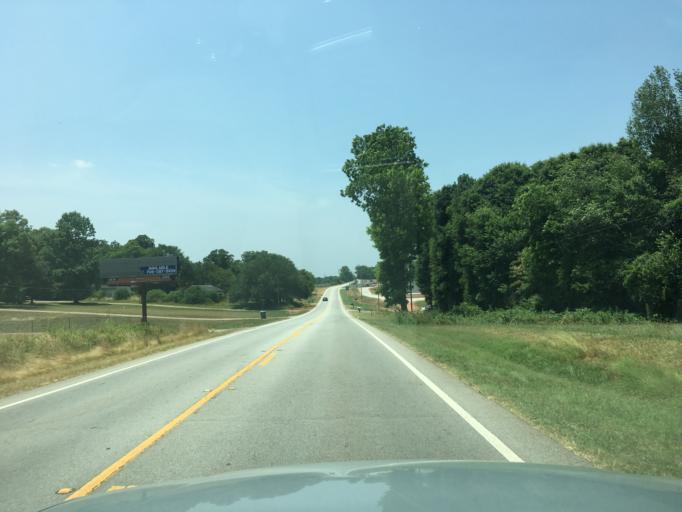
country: US
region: Georgia
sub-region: Hart County
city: Royston
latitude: 34.2891
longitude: -83.0855
